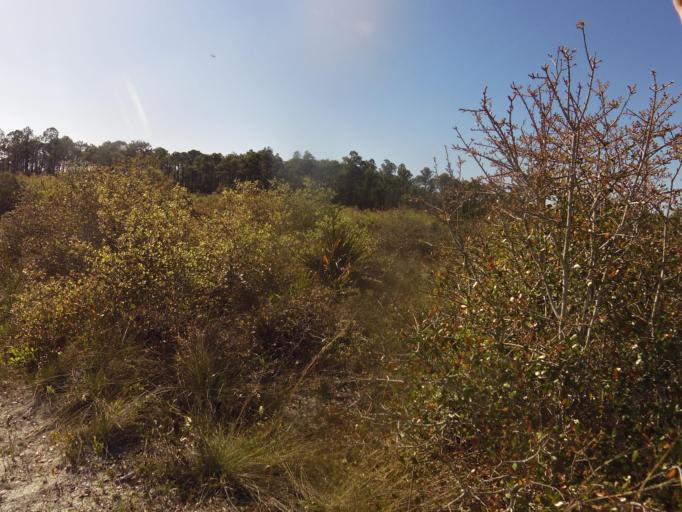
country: US
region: Florida
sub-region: Duval County
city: Atlantic Beach
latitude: 30.4732
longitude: -81.4904
